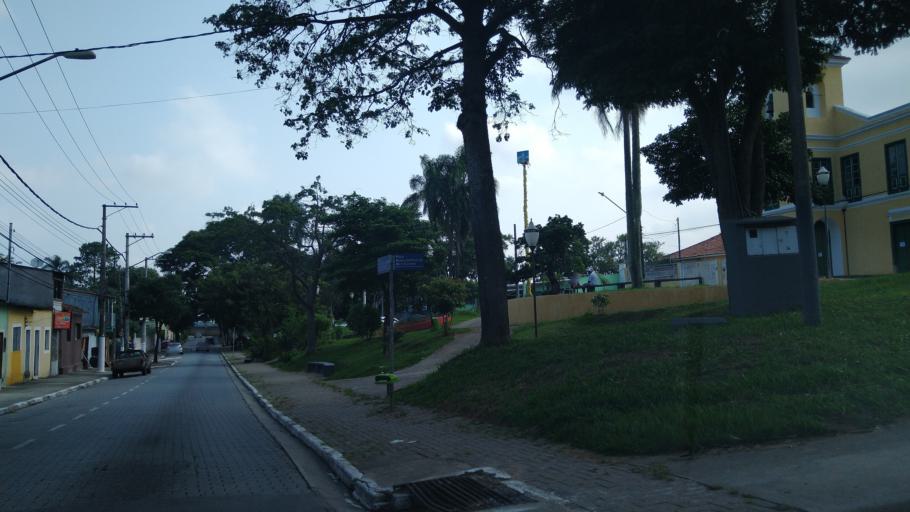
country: BR
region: Sao Paulo
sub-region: Itaquaquecetuba
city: Itaquaquecetuba
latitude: -23.4197
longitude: -46.4071
